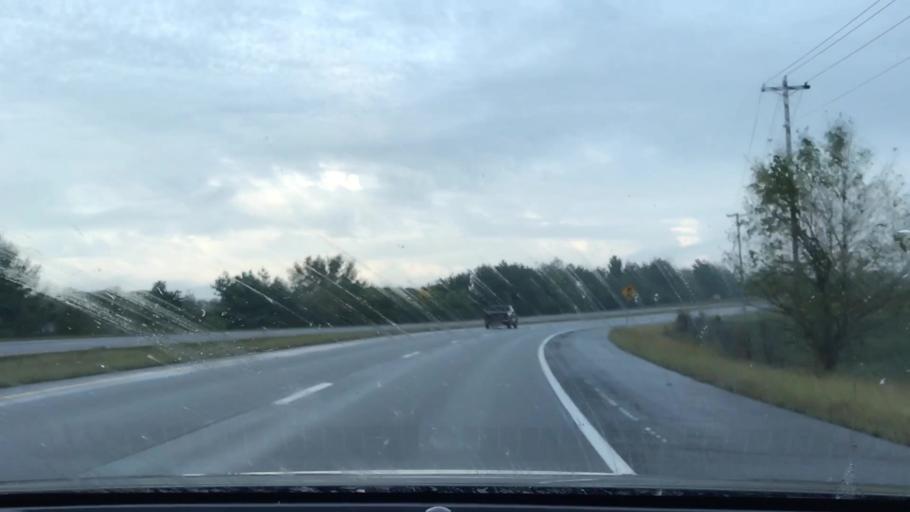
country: US
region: Tennessee
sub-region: Sumner County
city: Gallatin
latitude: 36.3943
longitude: -86.4797
